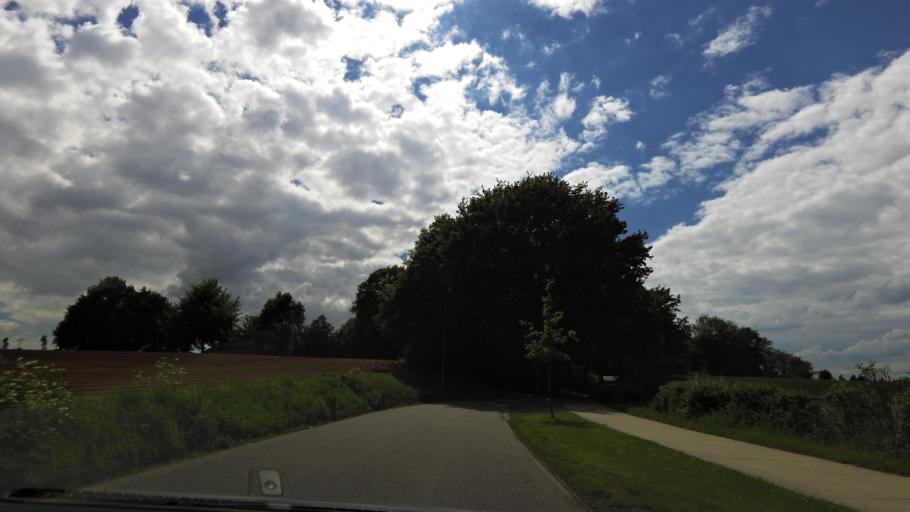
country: NL
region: Limburg
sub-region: Gemeente Schinnen
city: Oirsbeek
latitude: 50.9439
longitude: 5.9005
